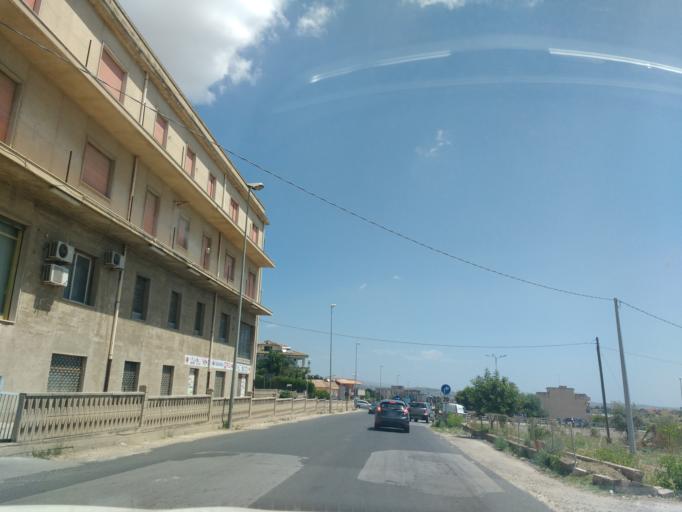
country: IT
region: Sicily
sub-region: Provincia di Siracusa
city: Rosolini
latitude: 36.8223
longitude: 14.9591
